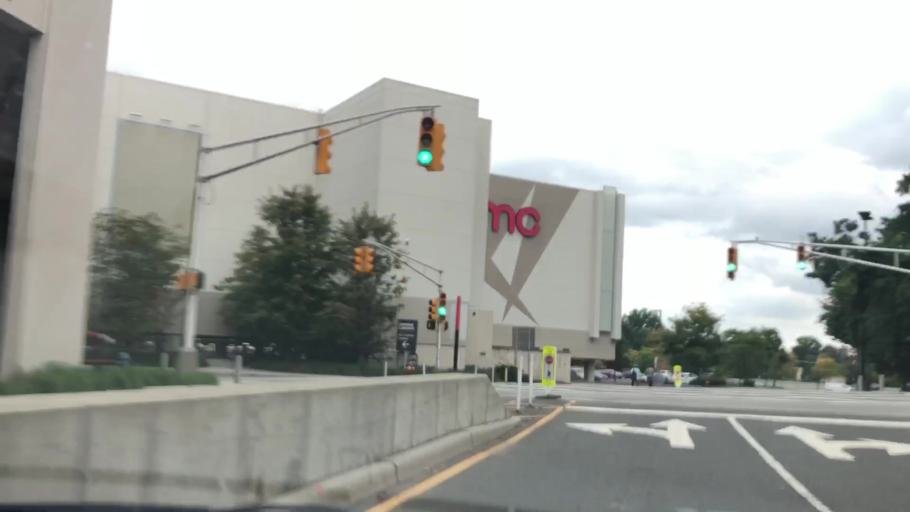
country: US
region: New Jersey
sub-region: Bergen County
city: Rochelle Park
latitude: 40.9156
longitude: -74.0782
